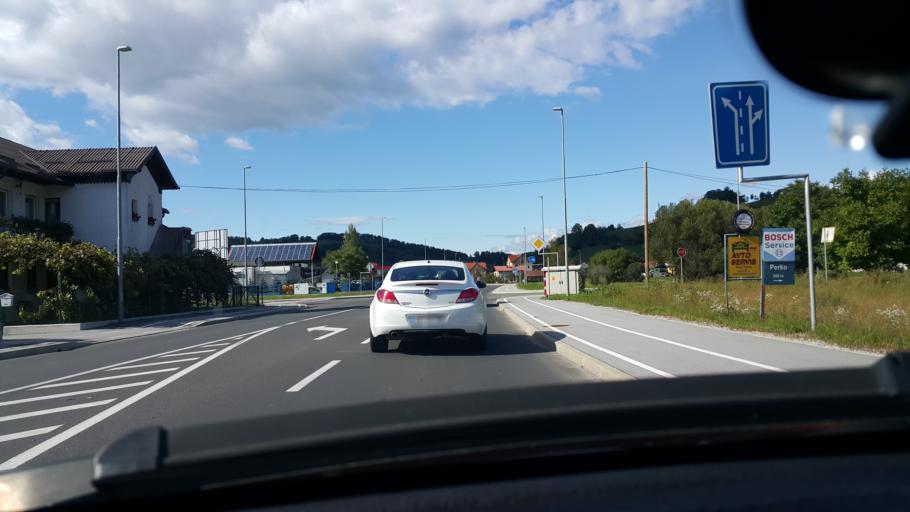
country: SI
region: Kungota
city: Zgornja Kungota
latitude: 46.6337
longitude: 15.6217
